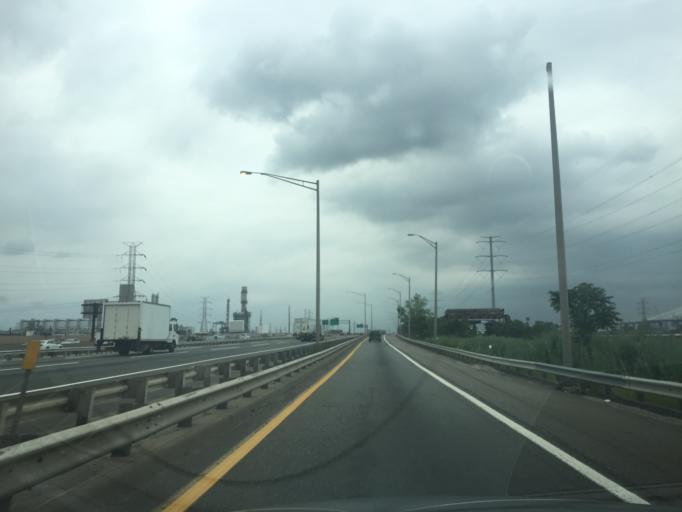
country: US
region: New Jersey
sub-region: Union County
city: Linden
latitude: 40.6262
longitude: -74.2148
